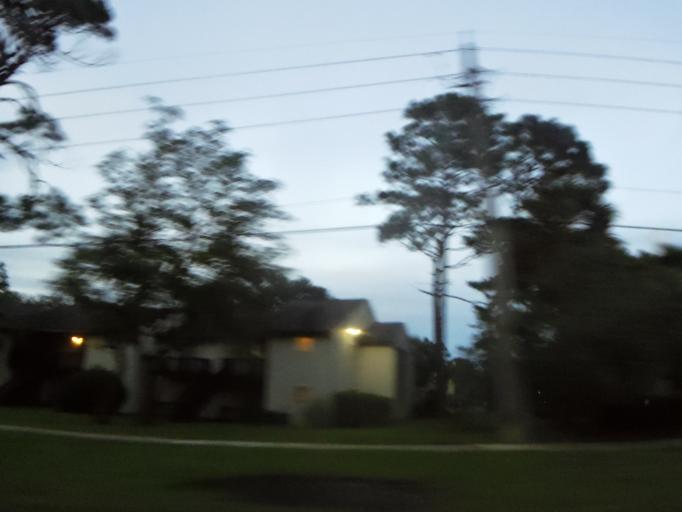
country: US
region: Florida
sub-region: Duval County
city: Jacksonville
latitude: 30.3776
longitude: -81.6070
